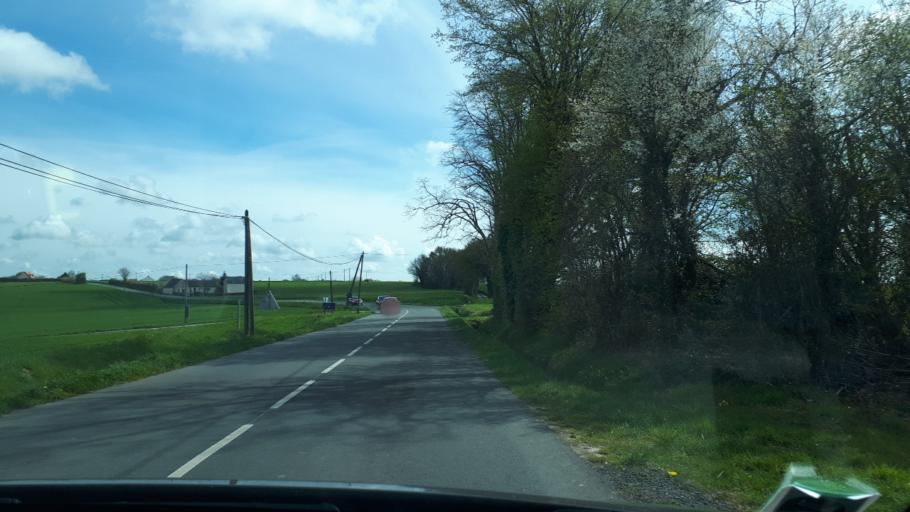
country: FR
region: Pays de la Loire
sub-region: Departement de la Sarthe
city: Le Grand-Luce
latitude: 47.8693
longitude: 0.4964
